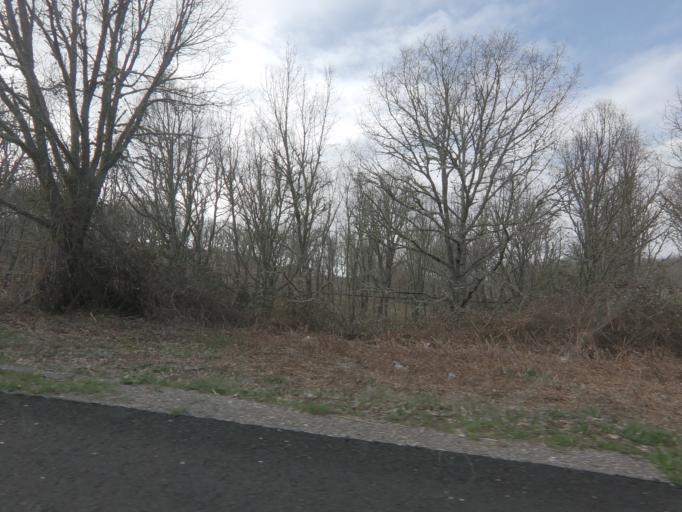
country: ES
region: Castille and Leon
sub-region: Provincia de Salamanca
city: Villasrubias
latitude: 40.3234
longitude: -6.6471
